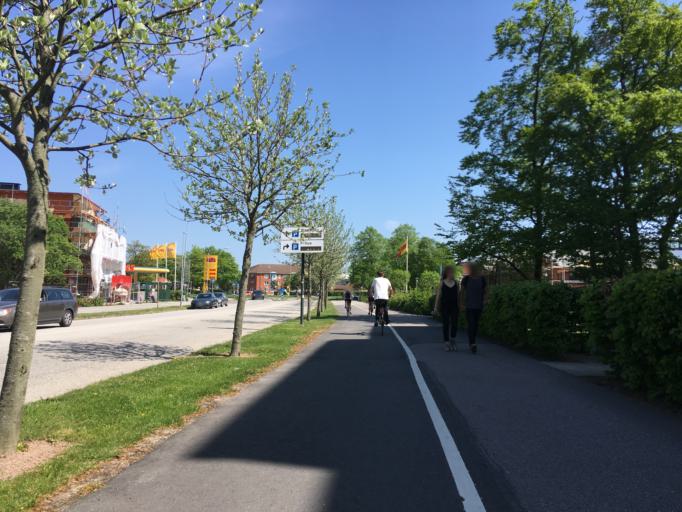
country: SE
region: Skane
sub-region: Lunds Kommun
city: Lund
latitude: 55.7026
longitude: 13.1747
